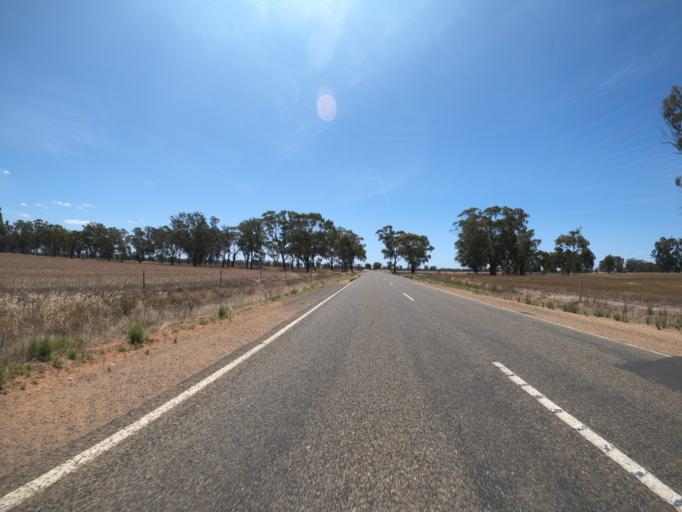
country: AU
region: Victoria
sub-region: Moira
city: Yarrawonga
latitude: -36.1802
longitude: 145.9672
